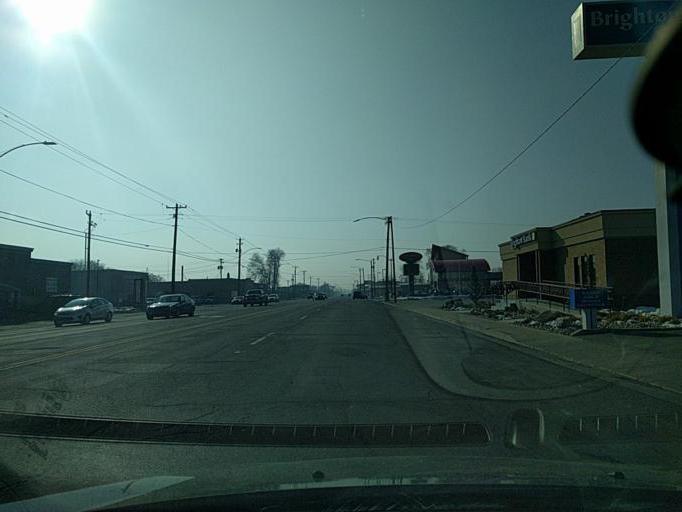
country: US
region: Utah
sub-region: Salt Lake County
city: South Salt Lake
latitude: 40.7389
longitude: -111.8998
